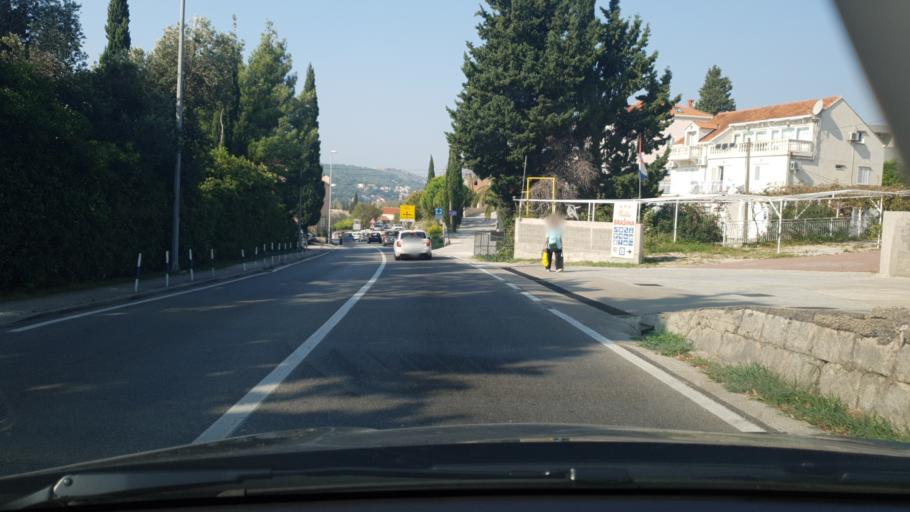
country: HR
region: Dubrovacko-Neretvanska
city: Cibaca
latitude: 42.6252
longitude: 18.1963
